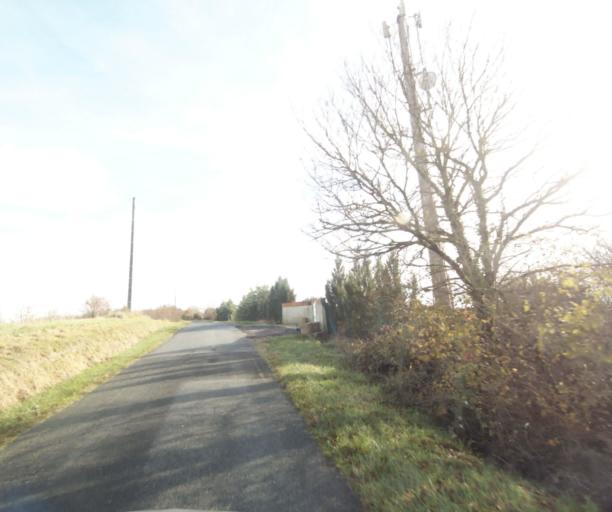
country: FR
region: Midi-Pyrenees
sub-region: Departement de la Haute-Garonne
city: Villemur-sur-Tarn
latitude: 43.8555
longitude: 1.5180
